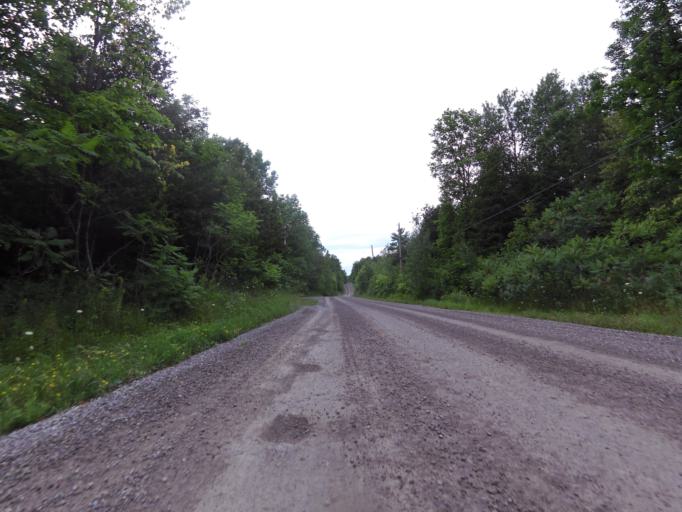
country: CA
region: Ontario
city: Carleton Place
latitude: 45.1479
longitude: -76.2298
